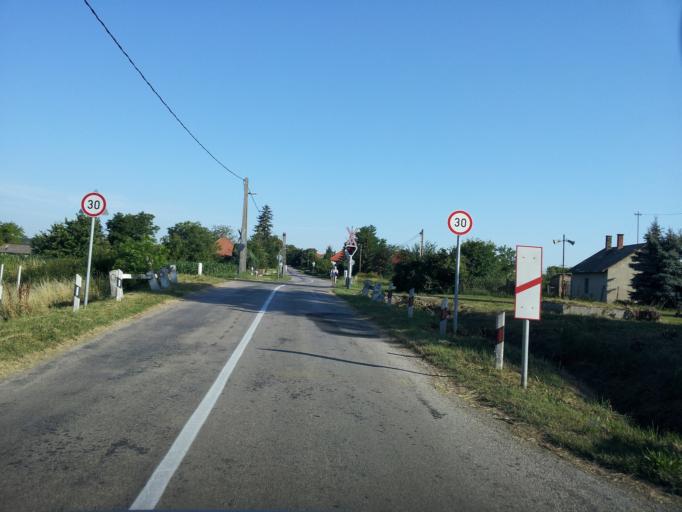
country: HU
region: Fejer
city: Polgardi
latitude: 47.0688
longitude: 18.2823
